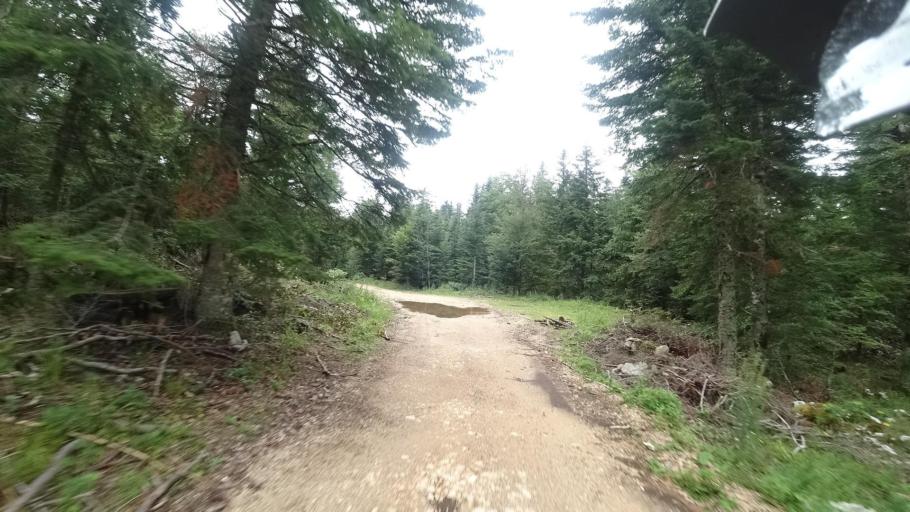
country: BA
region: Federation of Bosnia and Herzegovina
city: Bihac
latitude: 44.6210
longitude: 15.8074
